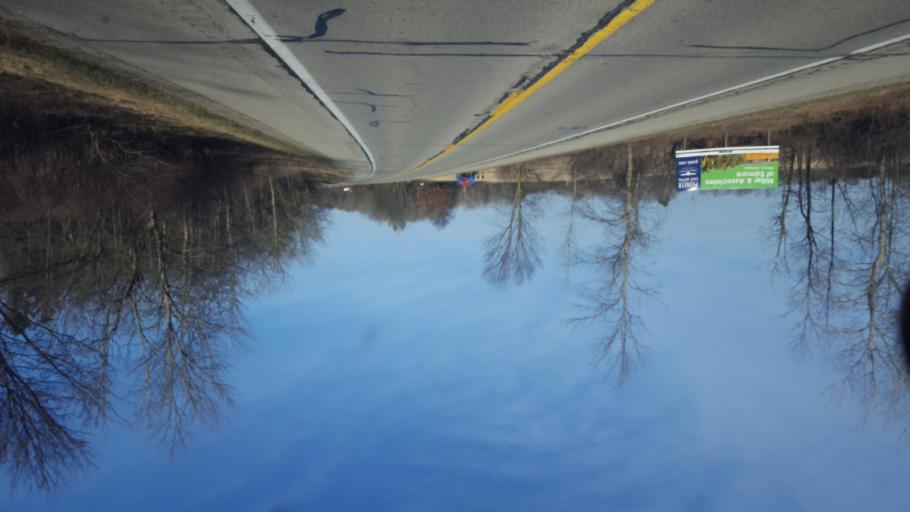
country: US
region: Michigan
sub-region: Montcalm County
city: Edmore
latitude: 43.4091
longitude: -85.1166
